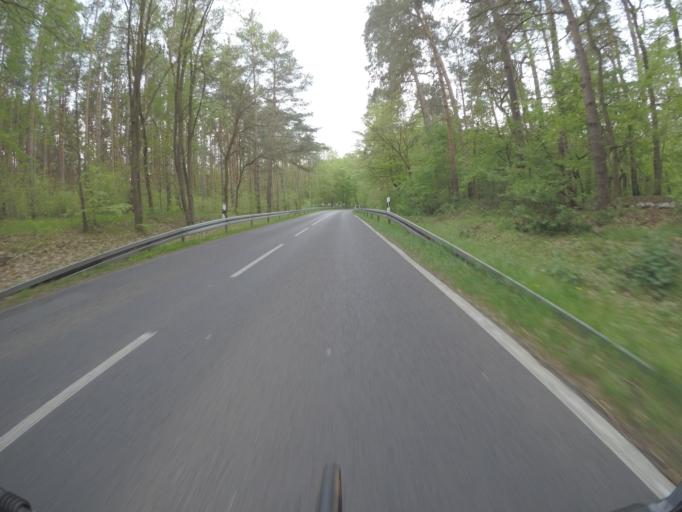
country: DE
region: Brandenburg
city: Joachimsthal
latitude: 52.9209
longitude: 13.7299
